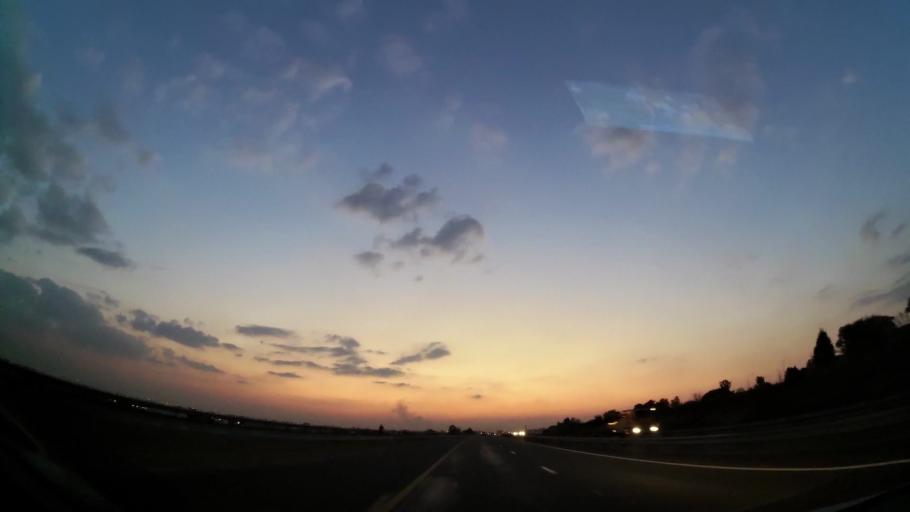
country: ZA
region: Gauteng
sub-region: Ekurhuleni Metropolitan Municipality
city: Springs
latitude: -26.2732
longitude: 28.3722
